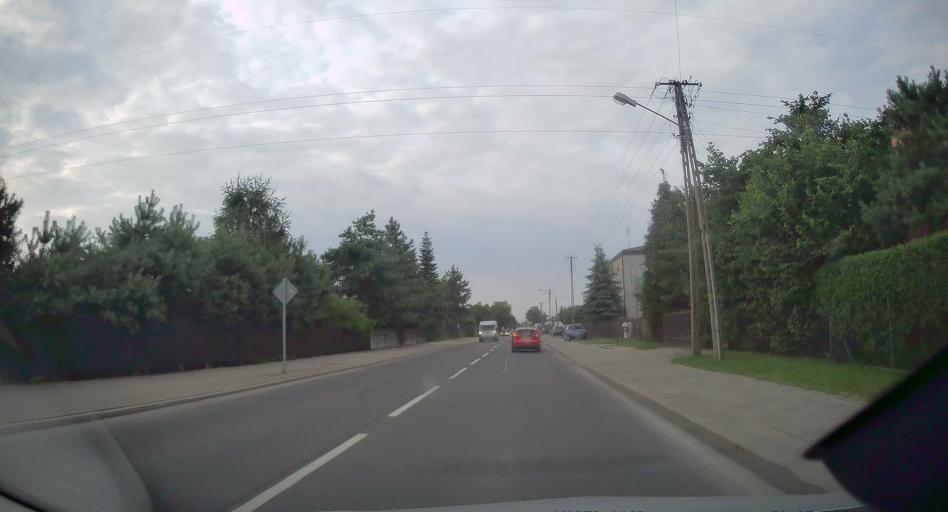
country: PL
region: Lodz Voivodeship
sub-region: Powiat radomszczanski
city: Radomsko
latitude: 51.0889
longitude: 19.4556
